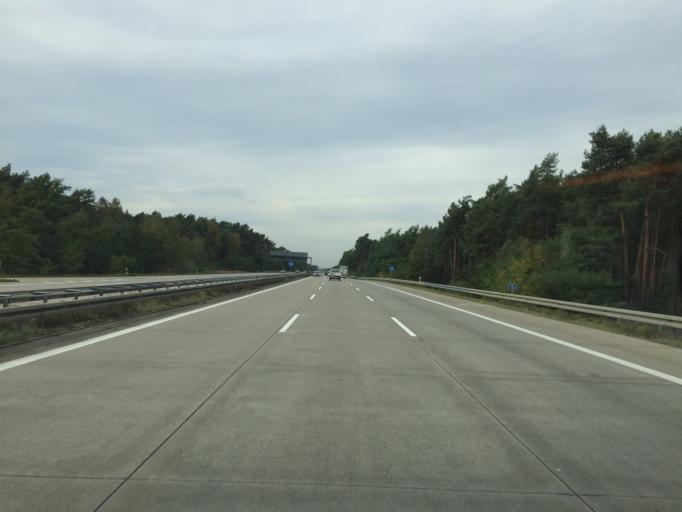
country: DE
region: Brandenburg
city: Brandenburg an der Havel
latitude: 52.3508
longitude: 12.5958
